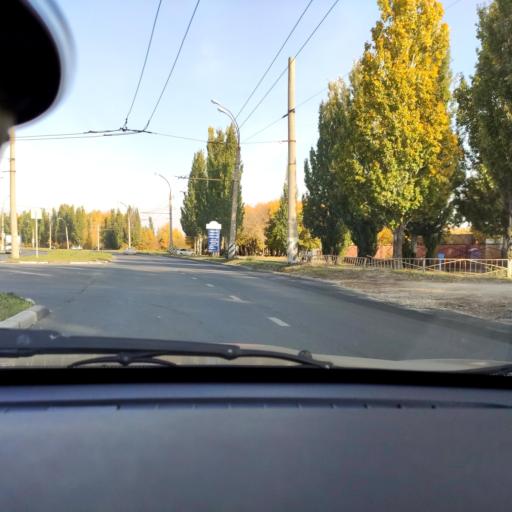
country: RU
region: Samara
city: Tol'yatti
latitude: 53.5417
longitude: 49.2794
